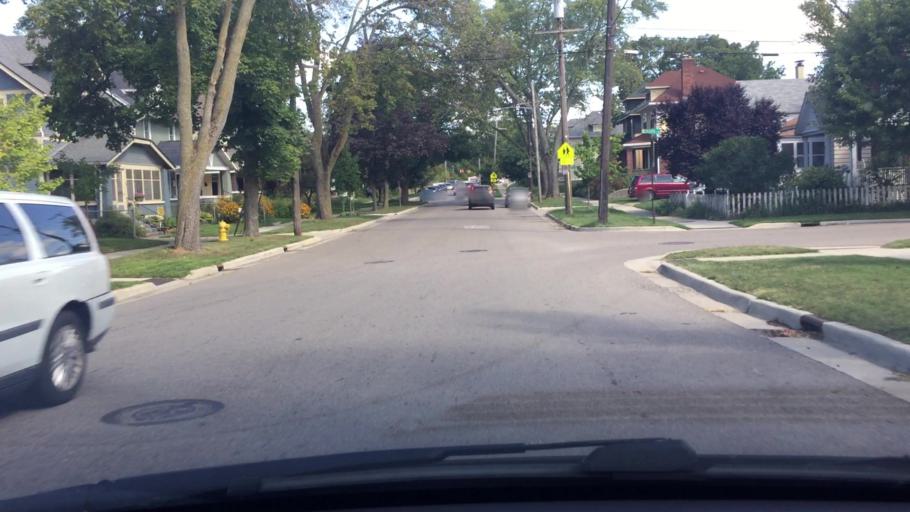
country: US
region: Michigan
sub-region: Kent County
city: East Grand Rapids
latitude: 42.9601
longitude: -85.6358
